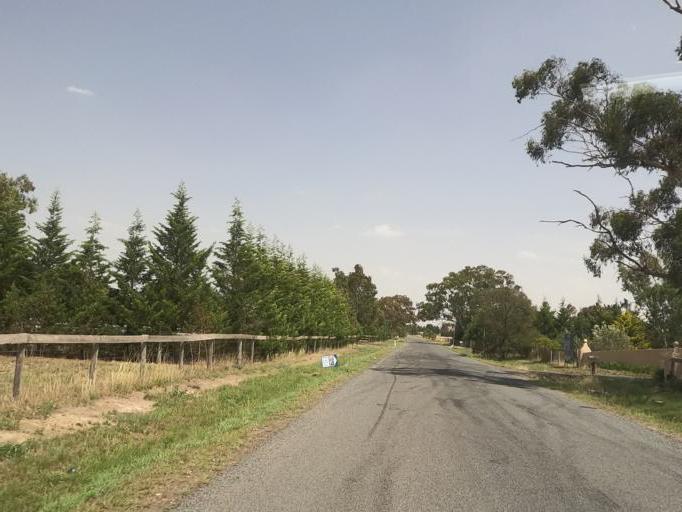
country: AU
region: Victoria
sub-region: Hume
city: Craigieburn
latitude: -37.5573
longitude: 144.8981
